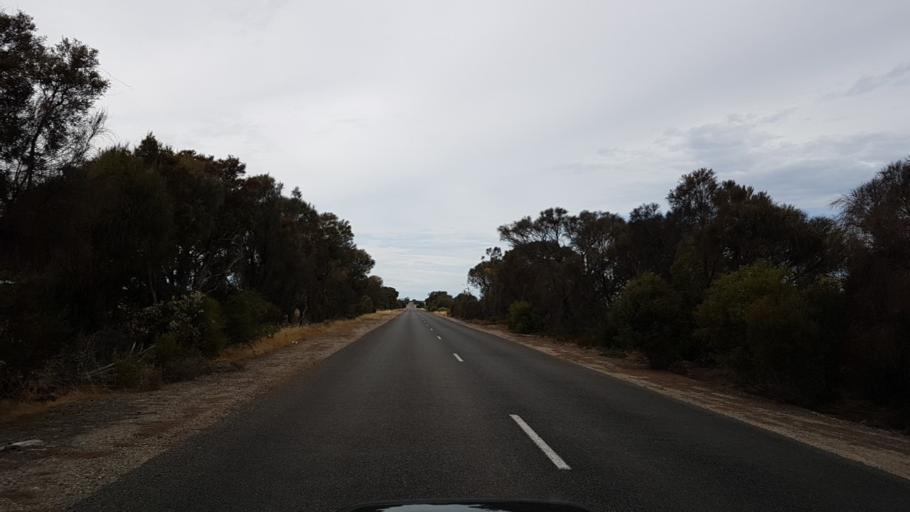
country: AU
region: South Australia
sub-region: Yorke Peninsula
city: Port Victoria
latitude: -34.9341
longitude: 137.0889
